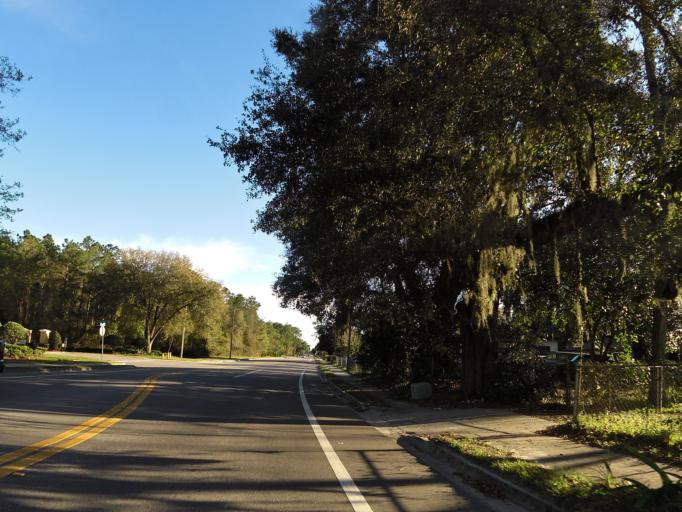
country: US
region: Florida
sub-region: Duval County
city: Jacksonville
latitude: 30.4581
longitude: -81.6132
